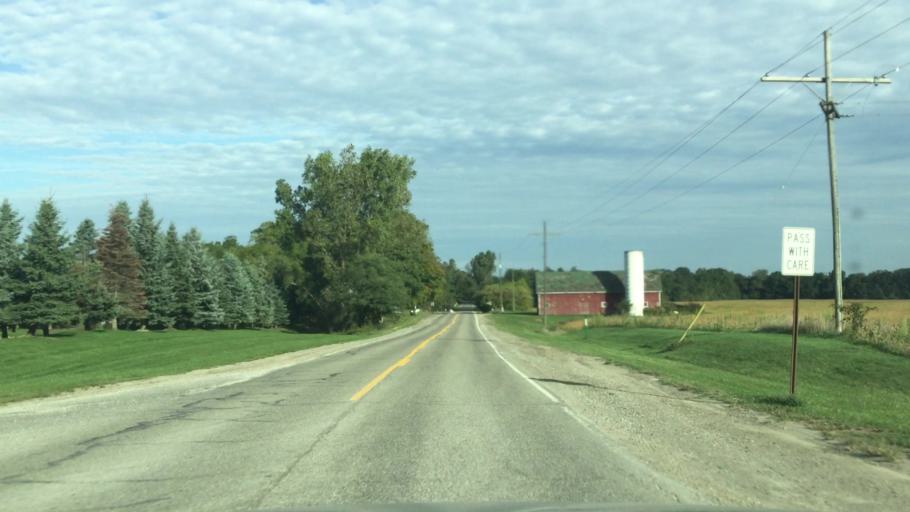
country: US
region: Michigan
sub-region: Livingston County
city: Howell
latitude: 42.5556
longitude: -83.8856
